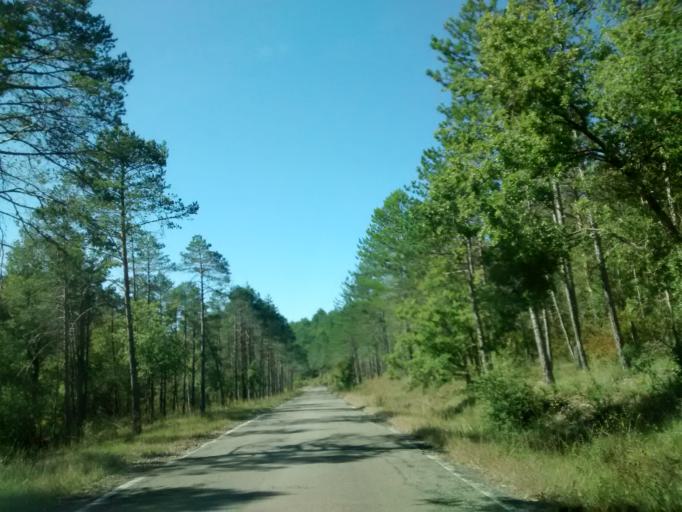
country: ES
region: Aragon
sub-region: Provincia de Huesca
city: Santa Cruz de la Seros
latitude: 42.4595
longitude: -0.6089
